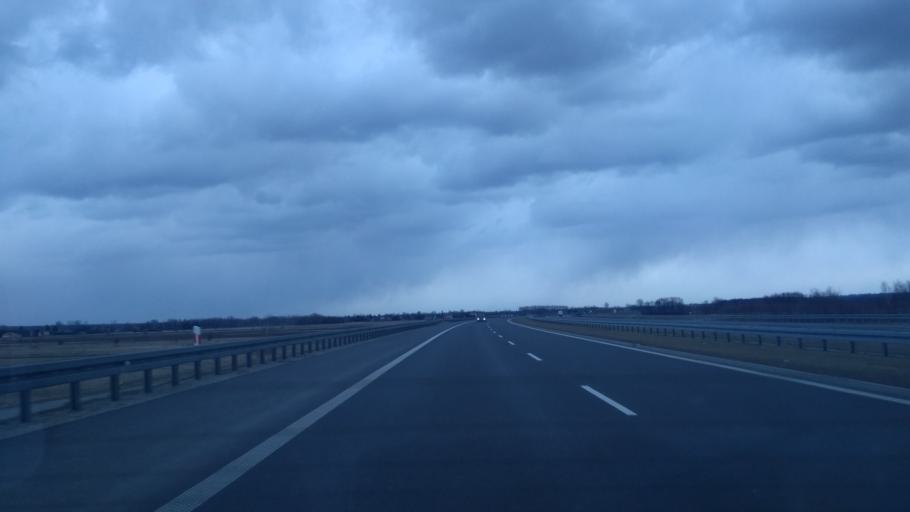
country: PL
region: Subcarpathian Voivodeship
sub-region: Powiat rzeszowski
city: Wolka Podlesna
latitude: 50.0959
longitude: 22.1128
